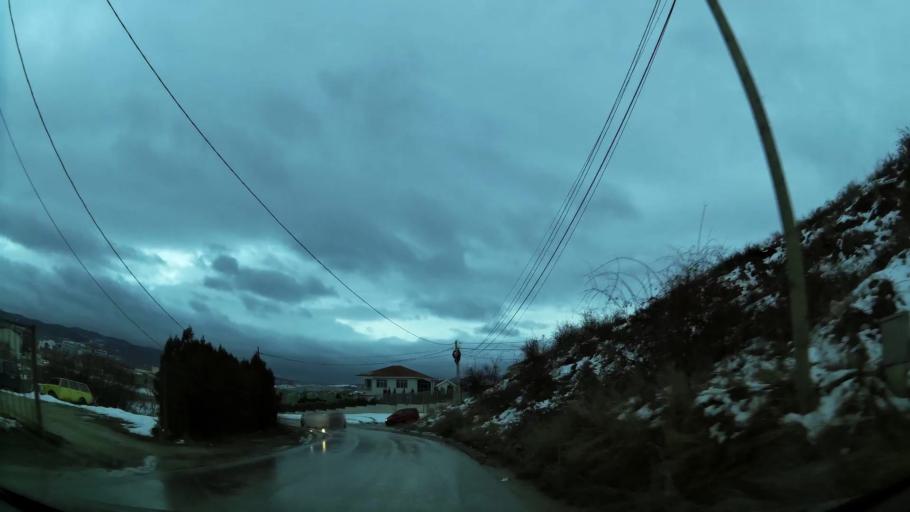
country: XK
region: Pristina
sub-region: Komuna e Prishtines
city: Pristina
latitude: 42.6291
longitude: 21.1650
